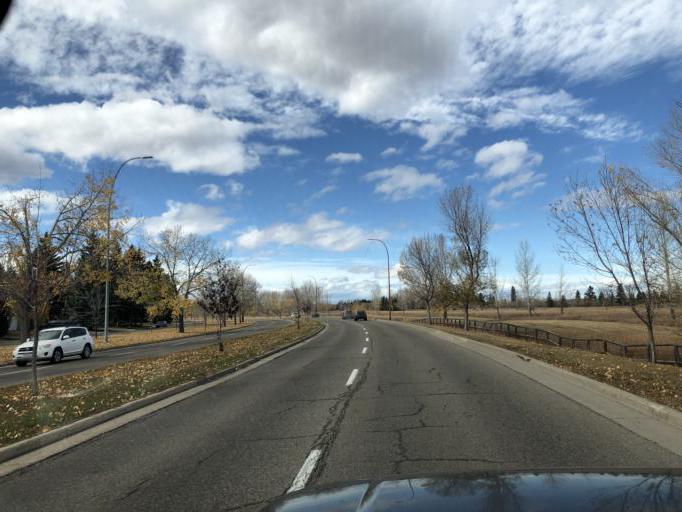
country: CA
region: Alberta
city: Calgary
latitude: 50.9745
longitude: -114.1265
